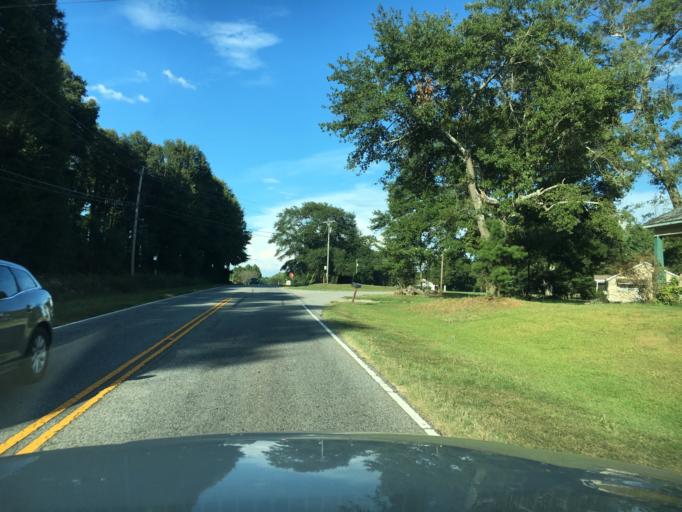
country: US
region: South Carolina
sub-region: Greenville County
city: Simpsonville
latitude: 34.7514
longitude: -82.2179
